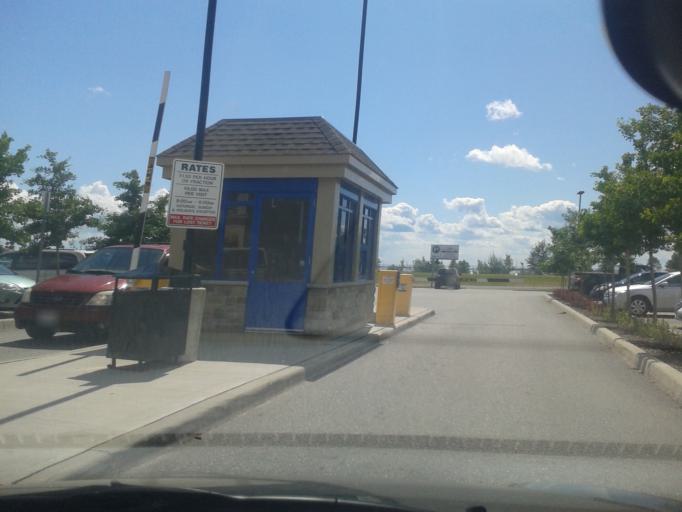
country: CA
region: Ontario
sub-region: Nipissing District
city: North Bay
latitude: 46.3112
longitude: -79.4659
